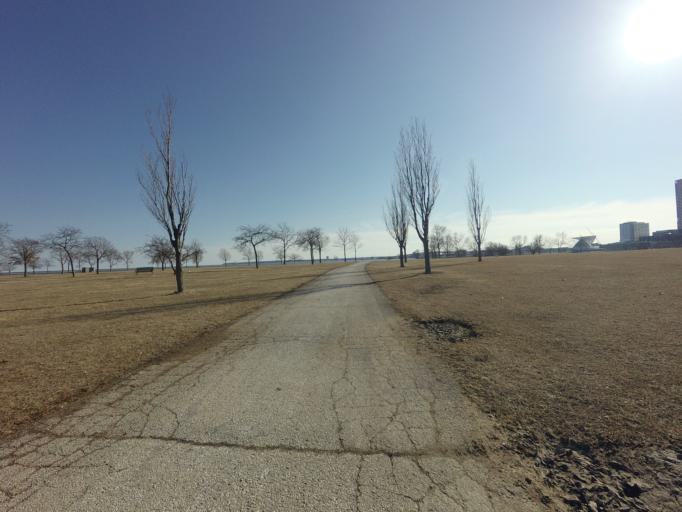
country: US
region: Wisconsin
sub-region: Milwaukee County
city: Milwaukee
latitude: 43.0446
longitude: -87.8905
